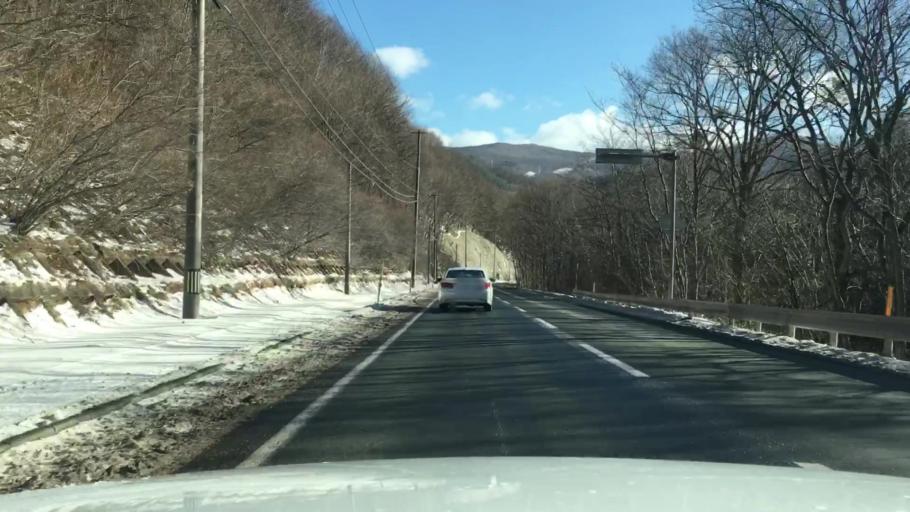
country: JP
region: Iwate
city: Morioka-shi
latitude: 39.6337
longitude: 141.4423
